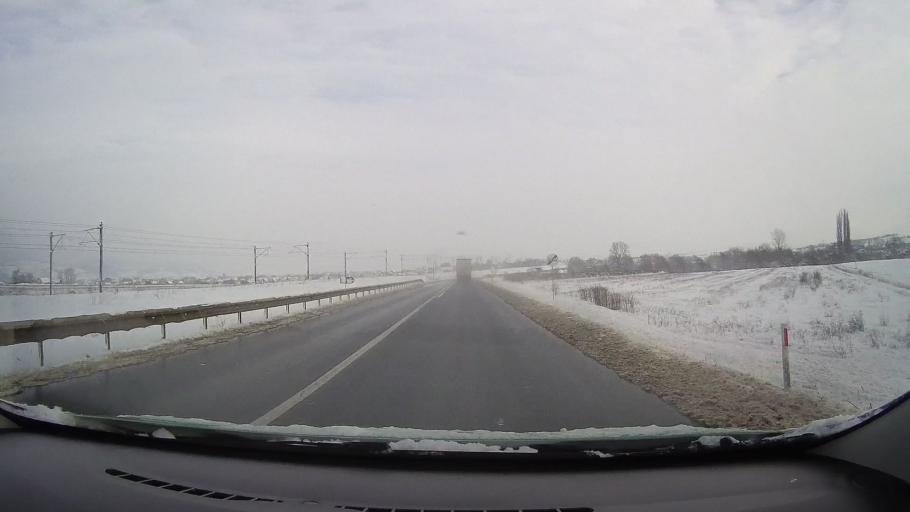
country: RO
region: Alba
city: Vurpar
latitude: 45.9819
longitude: 23.4795
